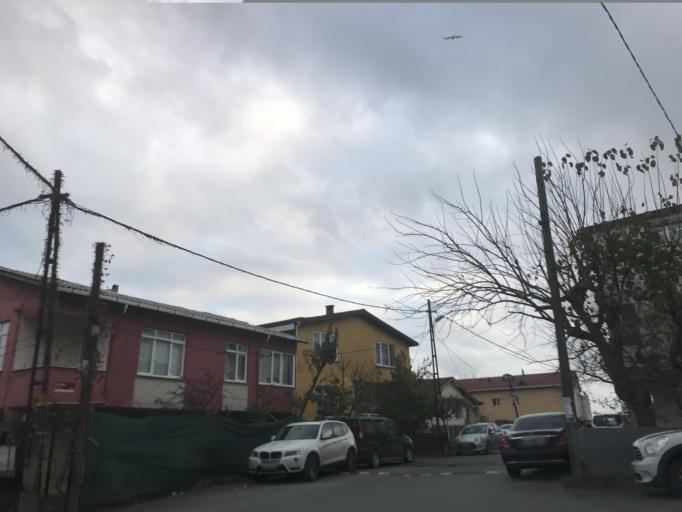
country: TR
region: Istanbul
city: Sisli
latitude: 41.1282
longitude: 29.0437
